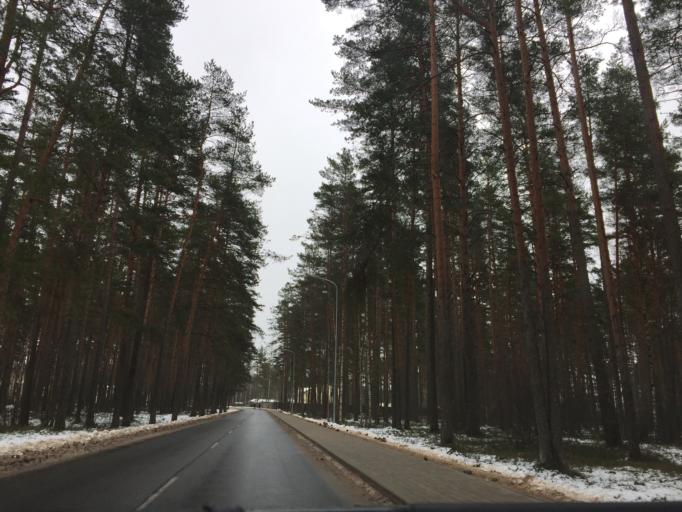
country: LV
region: Garkalne
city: Garkalne
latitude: 57.0422
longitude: 24.4252
